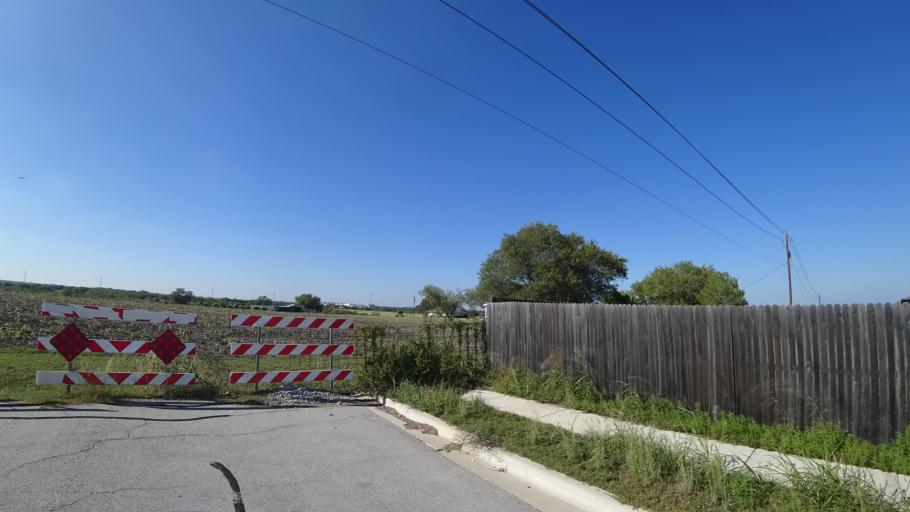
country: US
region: Texas
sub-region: Travis County
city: Manor
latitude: 30.3577
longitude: -97.6214
